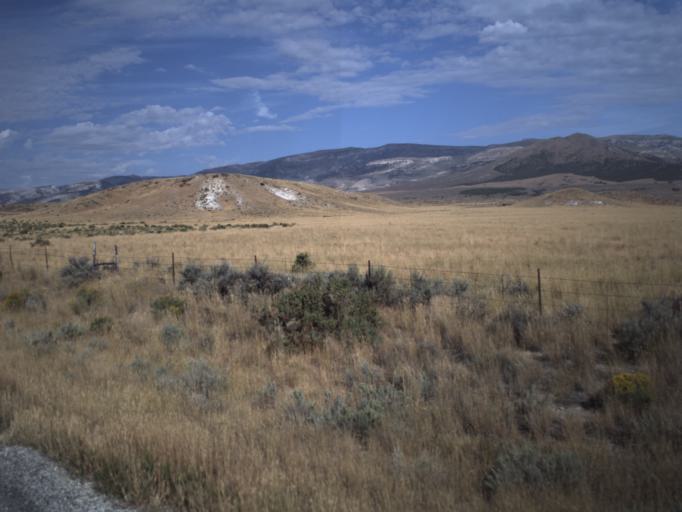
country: US
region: Idaho
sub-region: Cassia County
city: Burley
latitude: 41.8163
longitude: -113.2357
